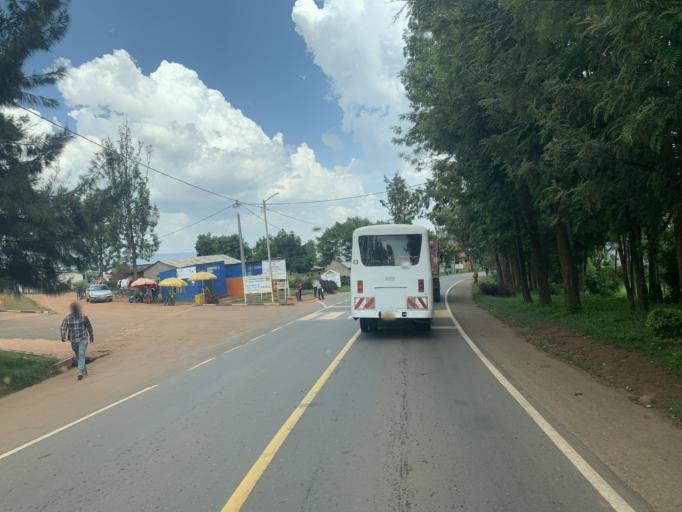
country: RW
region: Kigali
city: Kigali
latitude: -1.9944
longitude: 29.9150
